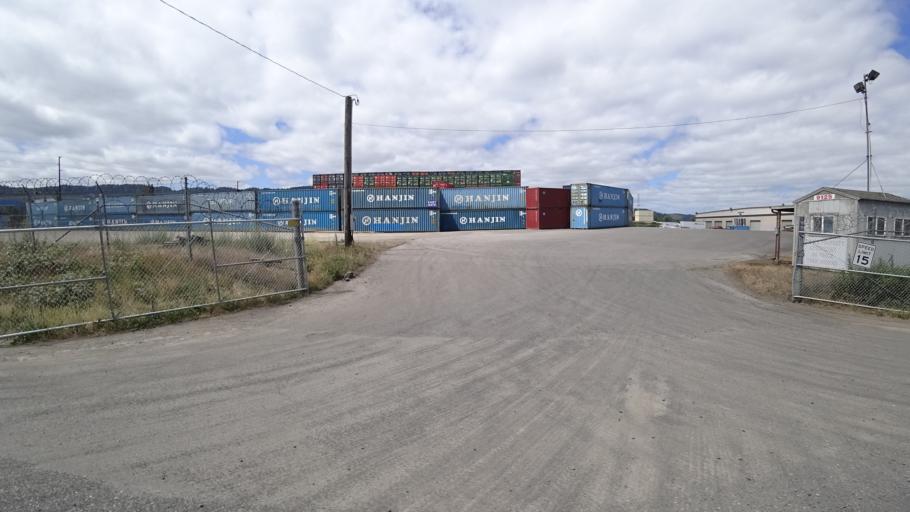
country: US
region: Oregon
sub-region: Washington County
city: West Haven
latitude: 45.6136
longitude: -122.7689
